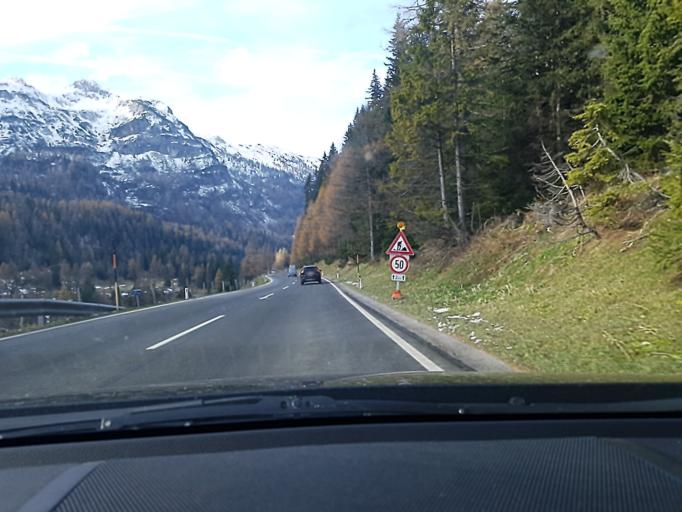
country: AT
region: Salzburg
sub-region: Politischer Bezirk Sankt Johann im Pongau
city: Untertauern
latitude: 47.2540
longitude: 13.5179
